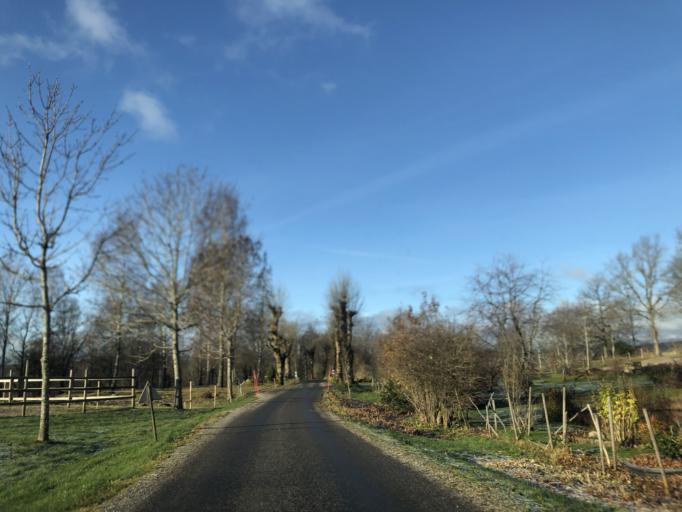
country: SE
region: Vaestra Goetaland
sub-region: Ulricehamns Kommun
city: Ulricehamn
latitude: 57.7251
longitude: 13.4119
